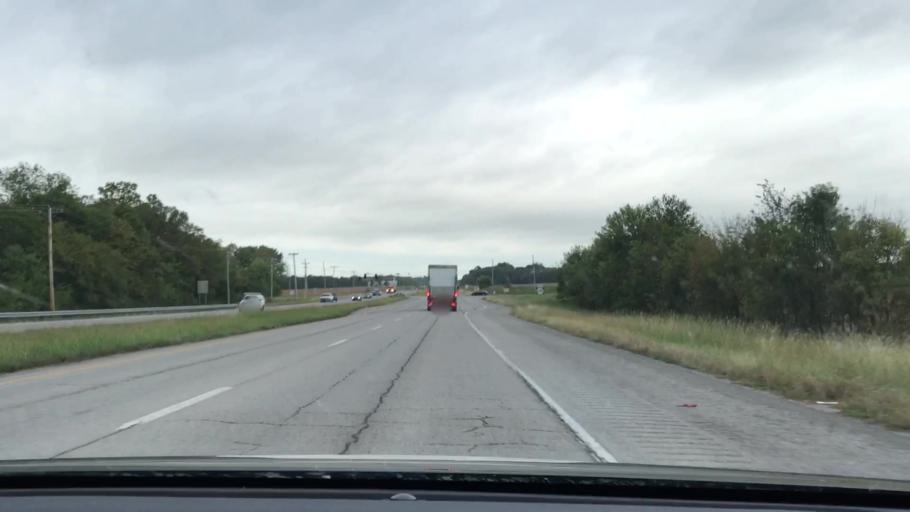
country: US
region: Kentucky
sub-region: Christian County
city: Hopkinsville
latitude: 36.8333
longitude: -87.5269
